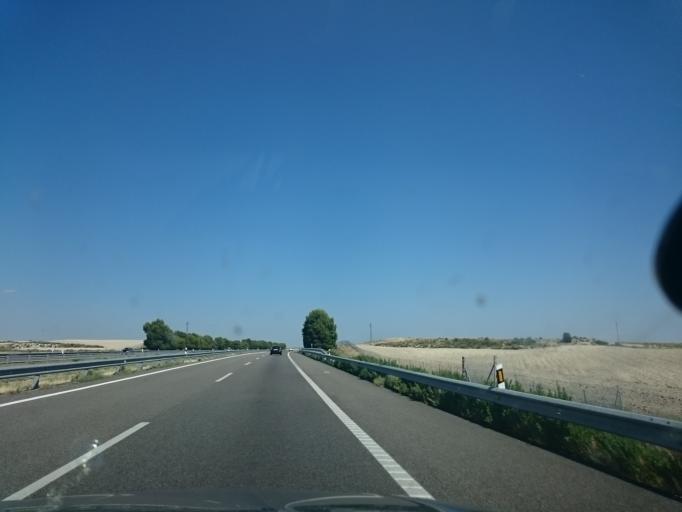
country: ES
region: Aragon
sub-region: Provincia de Zaragoza
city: Bujaraloz
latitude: 41.5189
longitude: -0.2418
